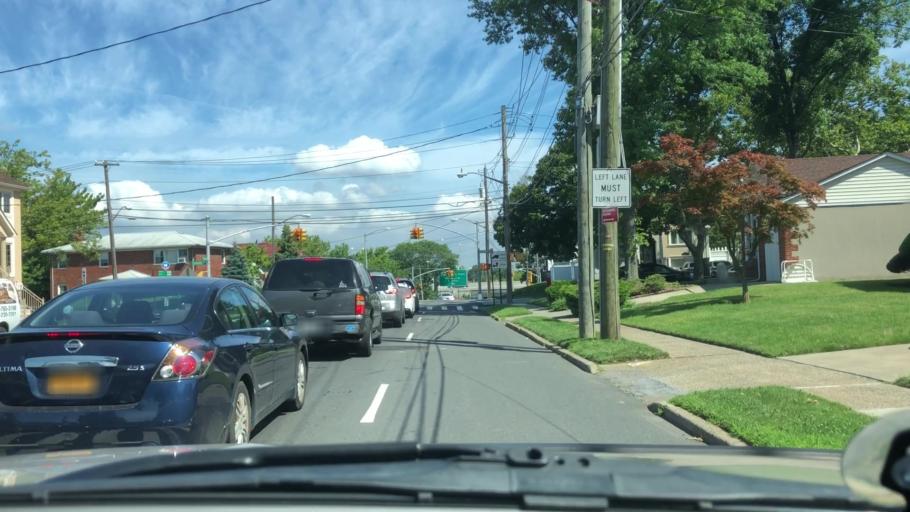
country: US
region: New York
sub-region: Richmond County
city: Staten Island
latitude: 40.6089
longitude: -74.1163
